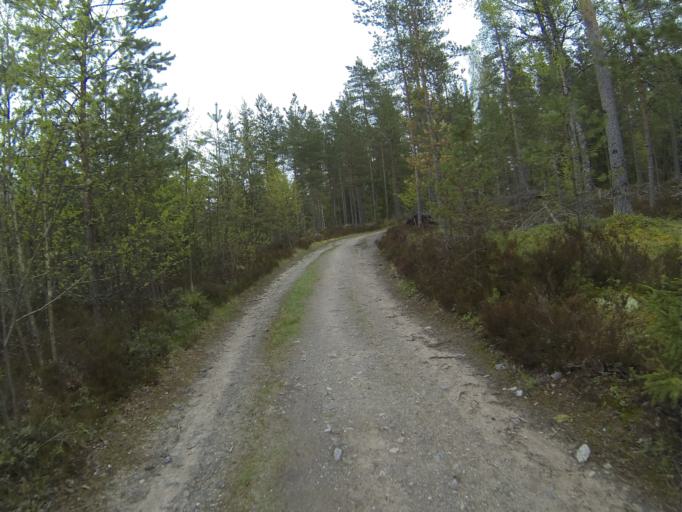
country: FI
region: Varsinais-Suomi
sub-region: Salo
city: Salo
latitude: 60.3978
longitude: 23.1975
